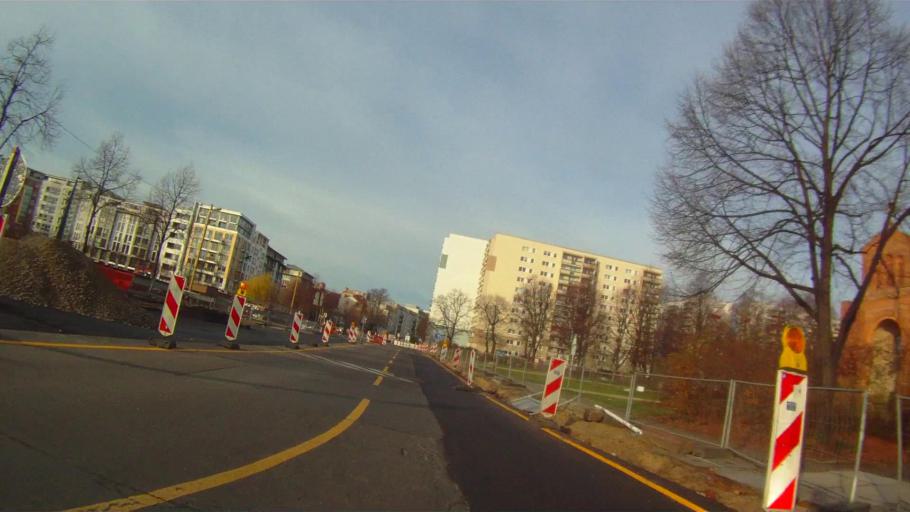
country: DE
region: Berlin
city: Bezirk Kreuzberg
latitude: 52.5062
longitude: 13.4198
